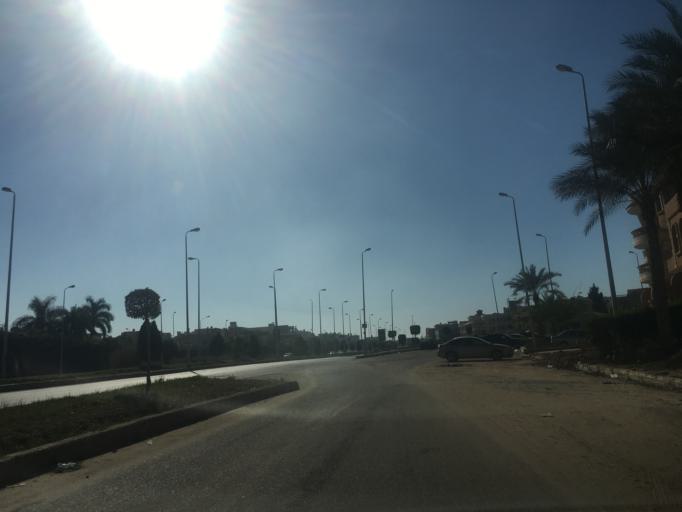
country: EG
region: Al Jizah
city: Awsim
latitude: 30.0249
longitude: 30.9851
